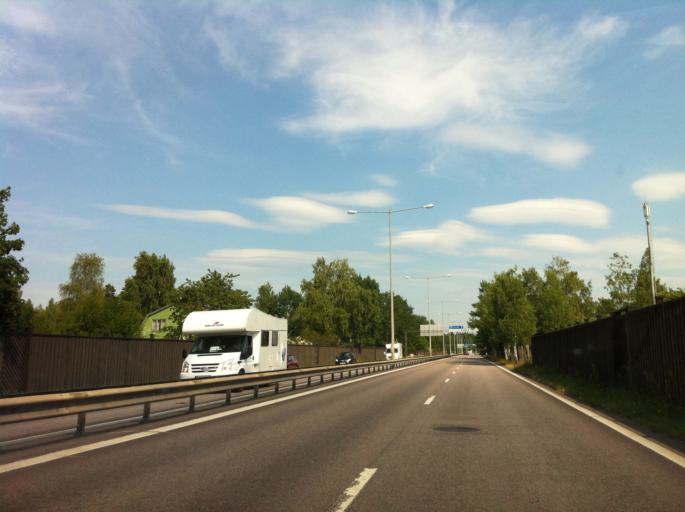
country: SE
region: Kalmar
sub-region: Nybro Kommun
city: Nybro
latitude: 56.7344
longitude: 15.9358
